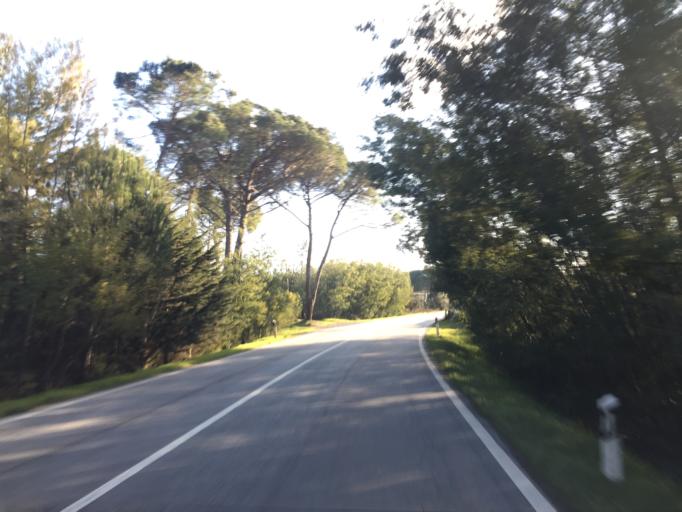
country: PT
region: Viseu
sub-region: Nelas
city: Nelas
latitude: 40.5030
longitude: -7.8898
